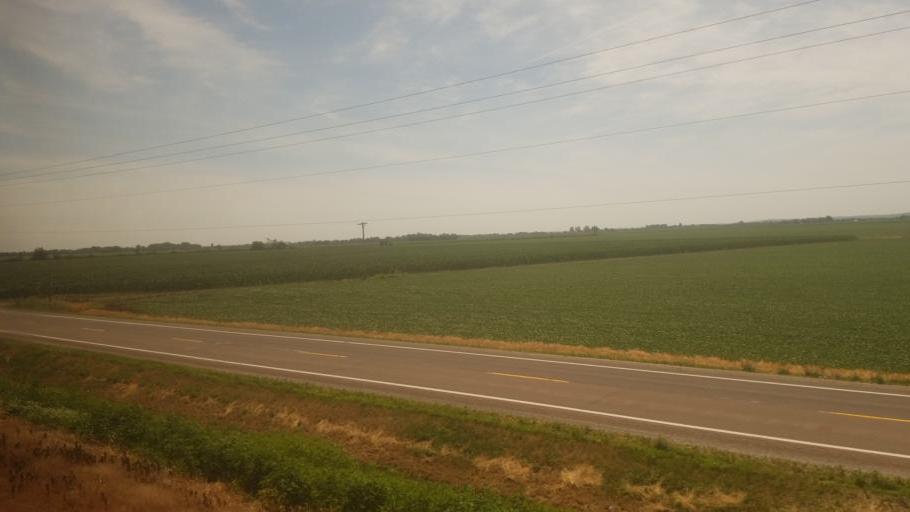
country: US
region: Missouri
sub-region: Carroll County
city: Carrollton
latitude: 39.3100
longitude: -93.6462
